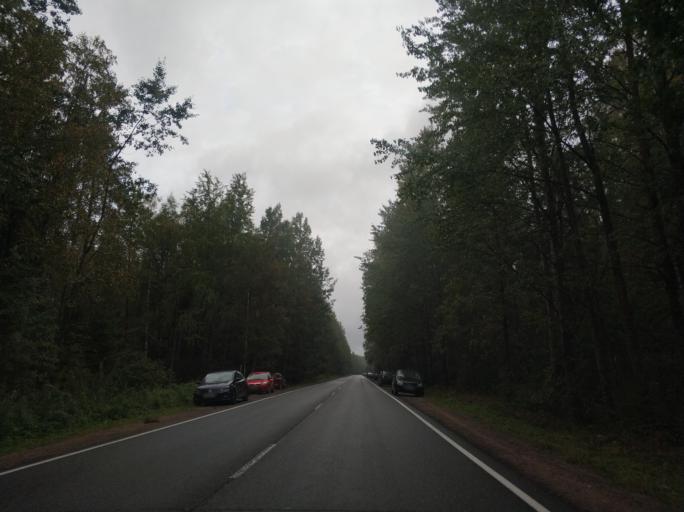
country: RU
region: Leningrad
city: Borisova Griva
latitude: 60.1560
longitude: 30.9297
